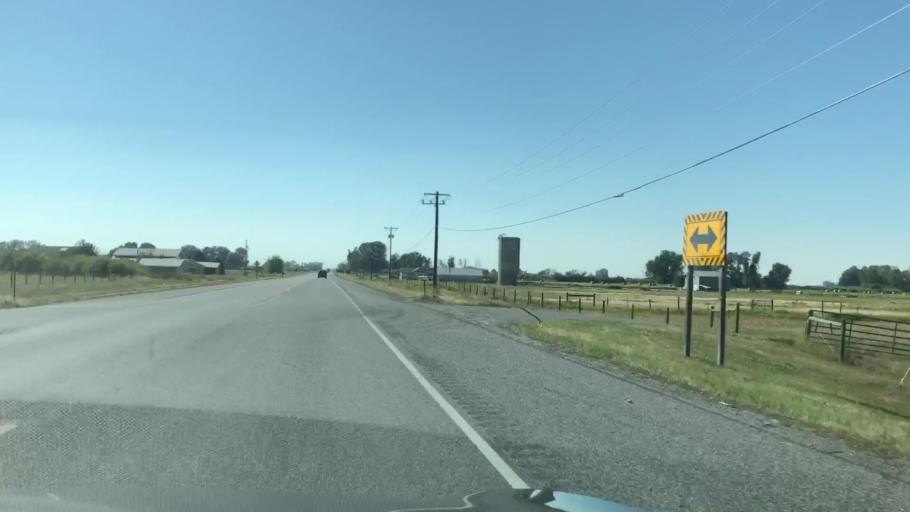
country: US
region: Montana
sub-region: Gallatin County
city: Belgrade
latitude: 45.7295
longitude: -111.1468
